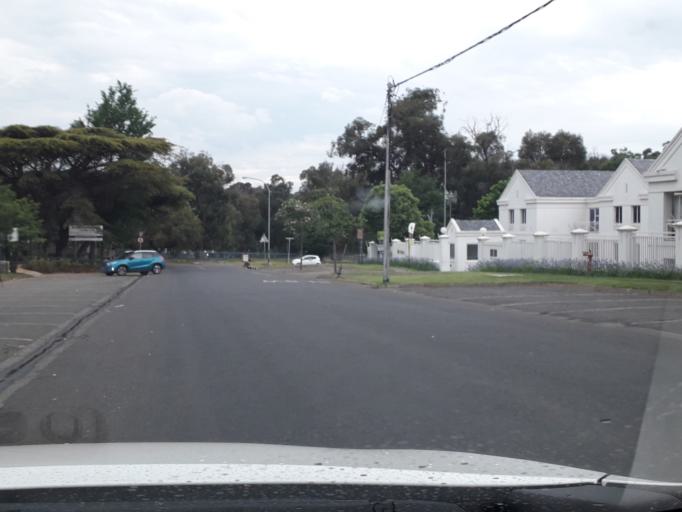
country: ZA
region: Gauteng
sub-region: City of Johannesburg Metropolitan Municipality
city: Johannesburg
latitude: -26.1370
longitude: 28.0577
